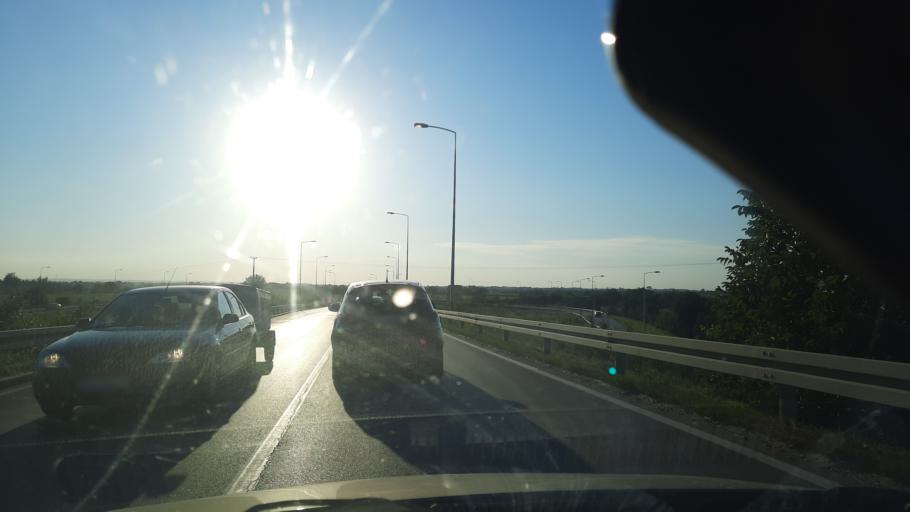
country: RS
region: Central Serbia
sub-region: Branicevski Okrug
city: Pozarevac
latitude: 44.5986
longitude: 21.1513
